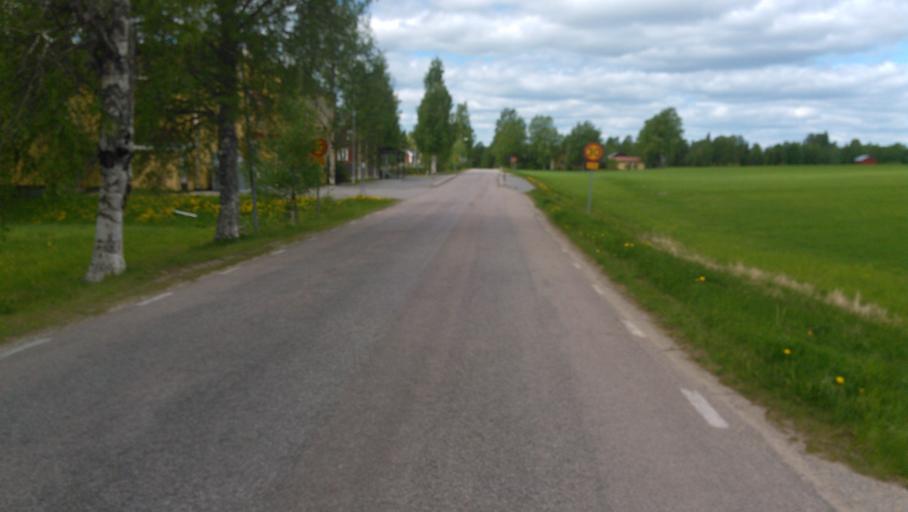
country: SE
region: Vaesterbotten
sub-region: Umea Kommun
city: Roback
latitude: 63.8677
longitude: 20.0731
